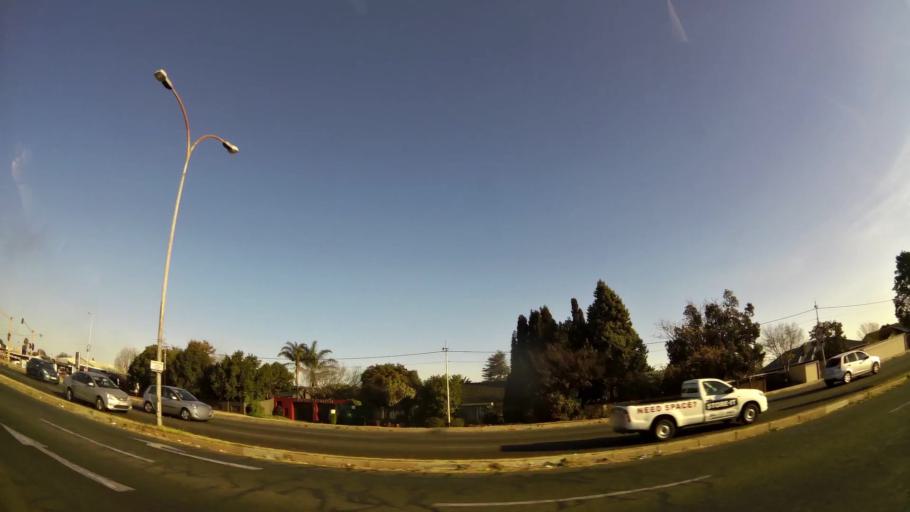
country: ZA
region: Gauteng
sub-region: City of Johannesburg Metropolitan Municipality
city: Roodepoort
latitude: -26.1452
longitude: 27.8804
